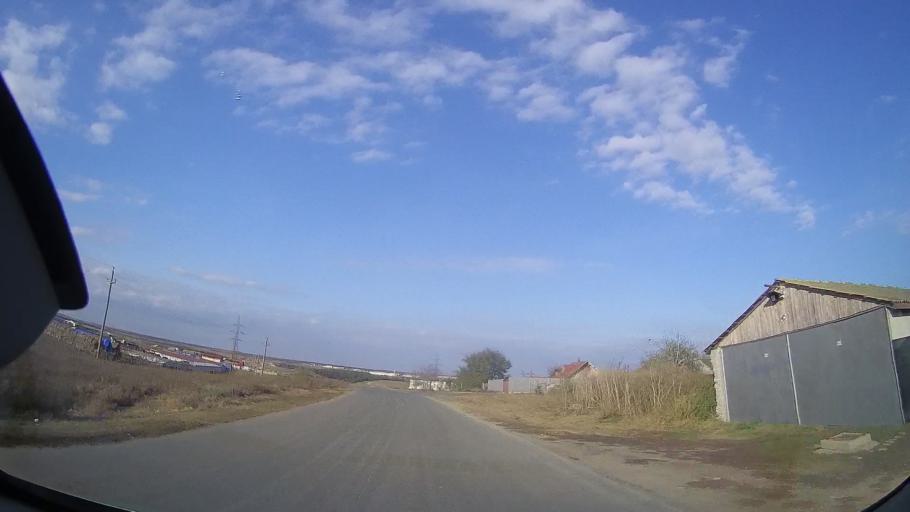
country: RO
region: Constanta
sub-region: Comuna Limanu
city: Limanu
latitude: 43.8004
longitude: 28.5221
